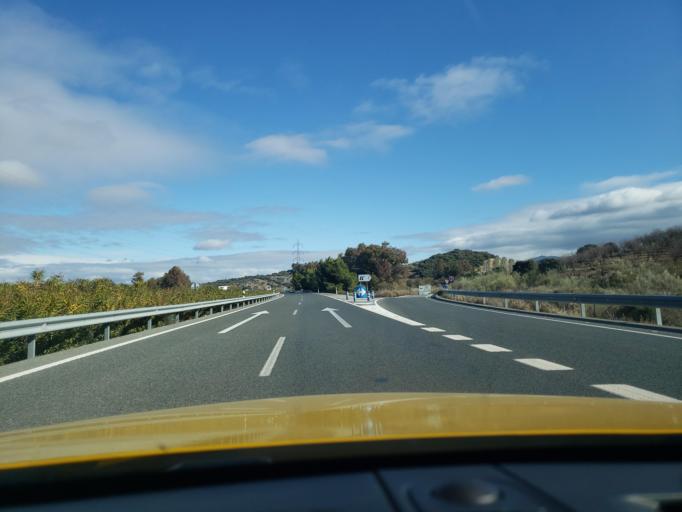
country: ES
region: Andalusia
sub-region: Provincia de Malaga
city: Villanueva de Tapia
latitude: 37.1169
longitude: -4.2987
